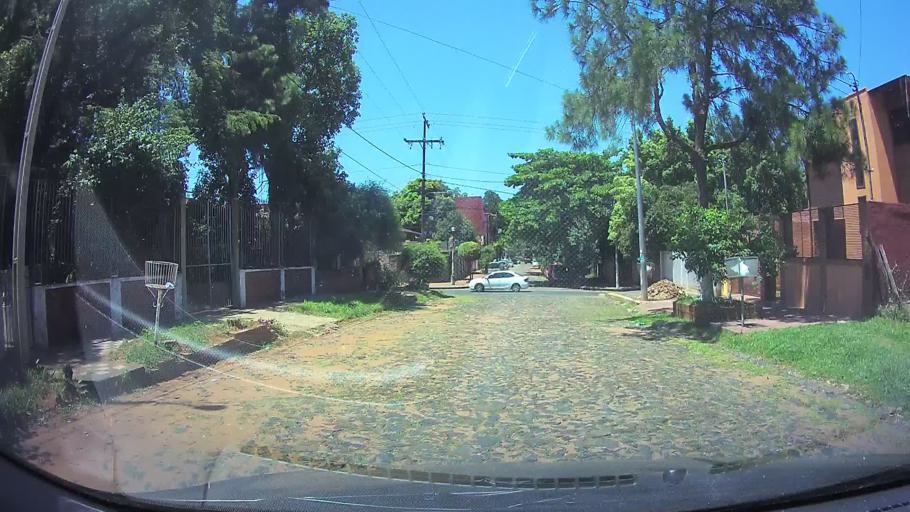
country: PY
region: Central
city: Lambare
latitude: -25.3208
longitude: -57.5905
